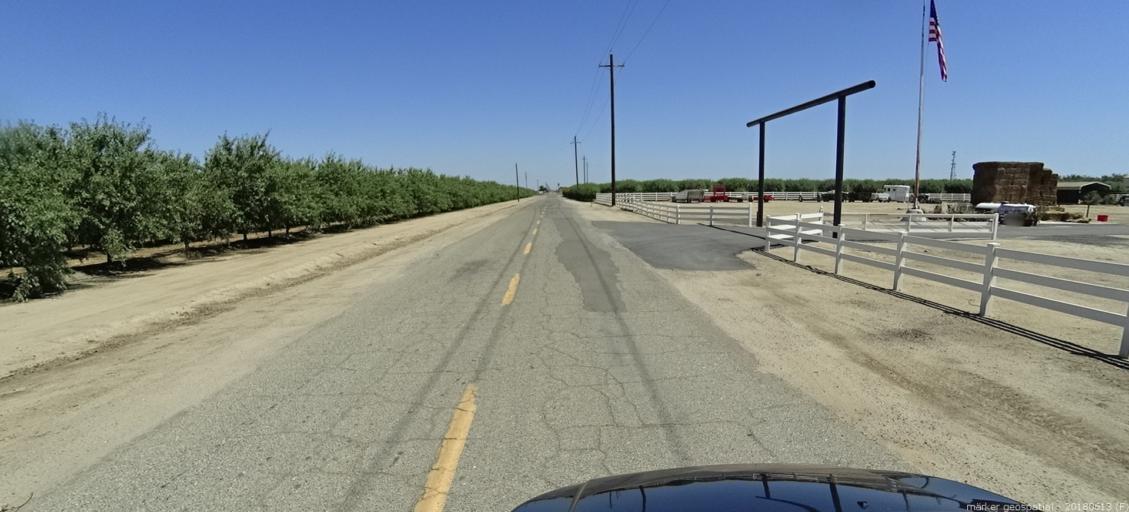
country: US
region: California
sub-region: Madera County
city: Chowchilla
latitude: 37.0799
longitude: -120.3289
